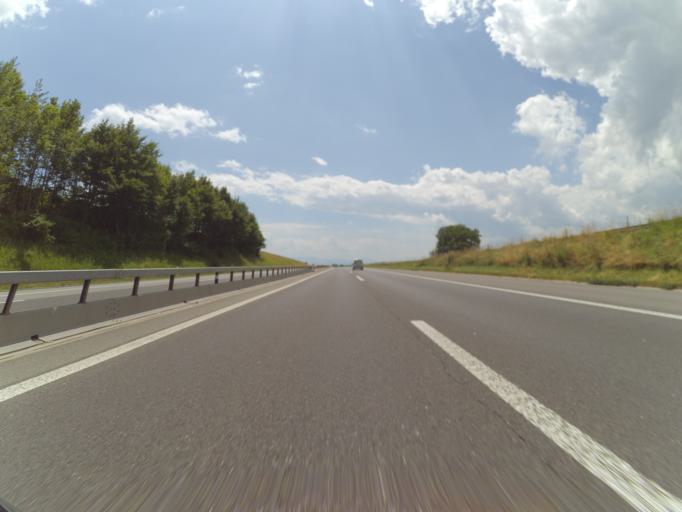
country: CH
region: Vaud
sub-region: Jura-Nord vaudois District
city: Bavois
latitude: 46.6401
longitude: 6.5625
